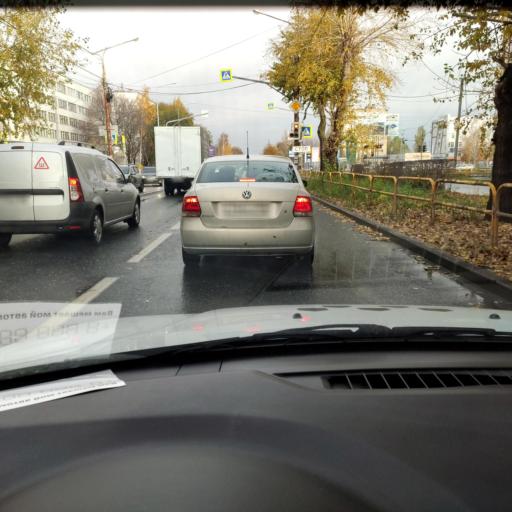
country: RU
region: Samara
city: Tol'yatti
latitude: 53.5371
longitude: 49.4101
